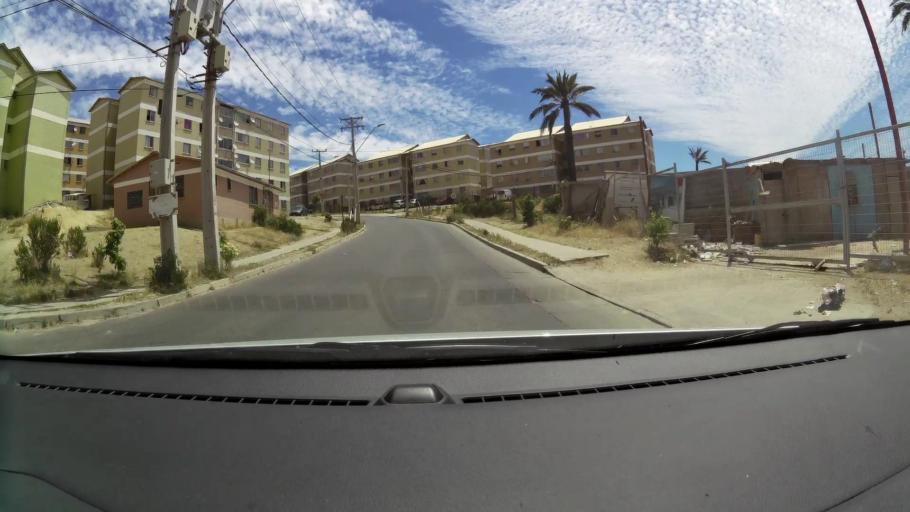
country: CL
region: Valparaiso
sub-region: Provincia de Valparaiso
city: Vina del Mar
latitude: -33.0623
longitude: -71.5633
